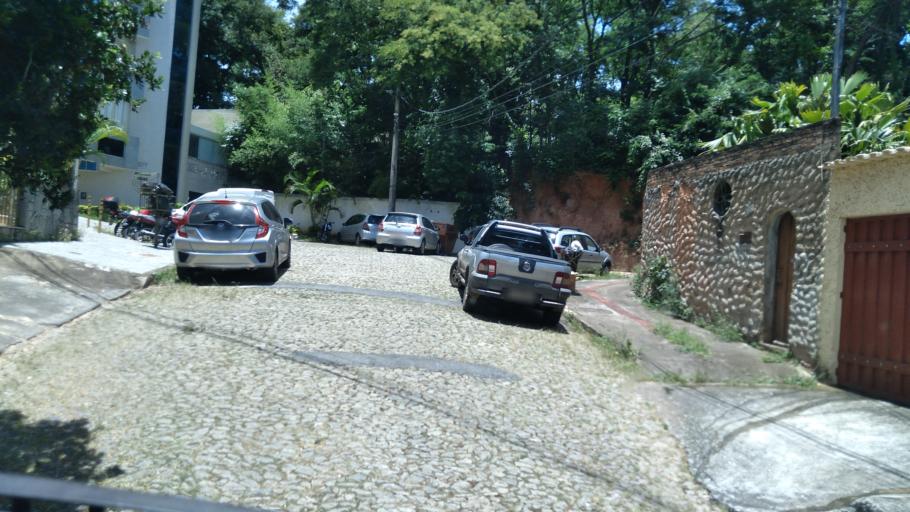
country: BR
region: Minas Gerais
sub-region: Belo Horizonte
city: Belo Horizonte
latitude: -19.9182
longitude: -43.9915
